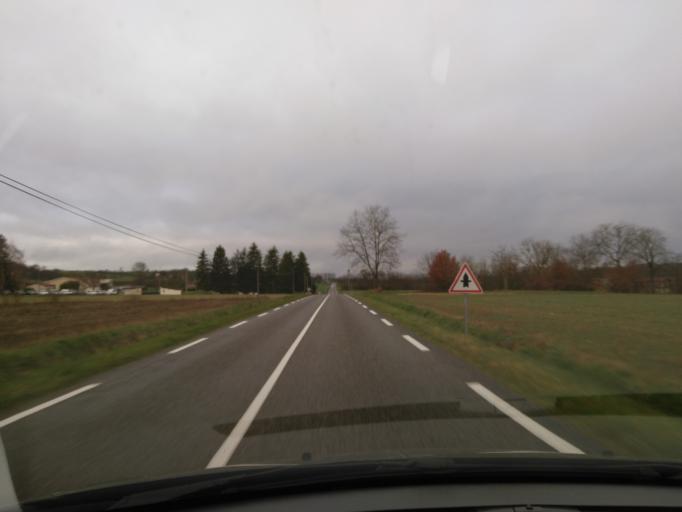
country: FR
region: Midi-Pyrenees
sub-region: Departement de la Haute-Garonne
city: Montesquieu-Volvestre
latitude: 43.1771
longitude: 1.2520
